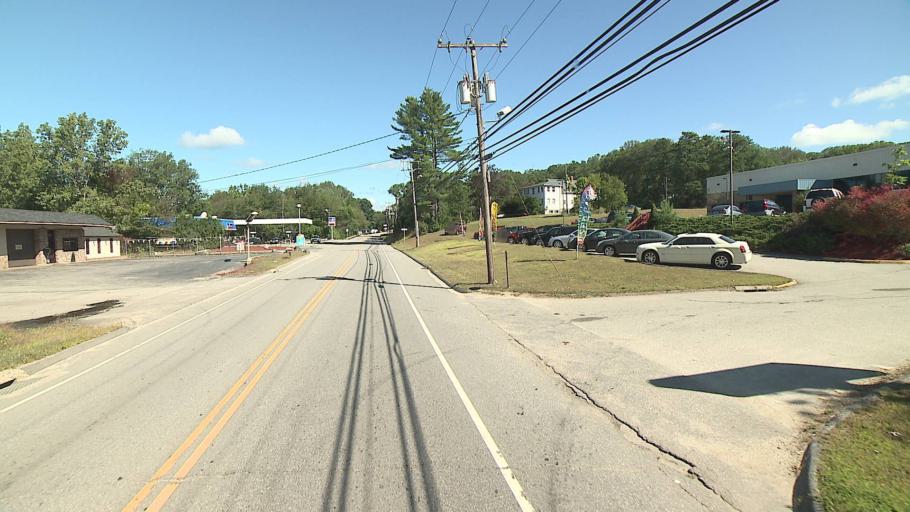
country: US
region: Connecticut
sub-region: Windham County
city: Wauregan
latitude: 41.7644
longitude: -71.9001
